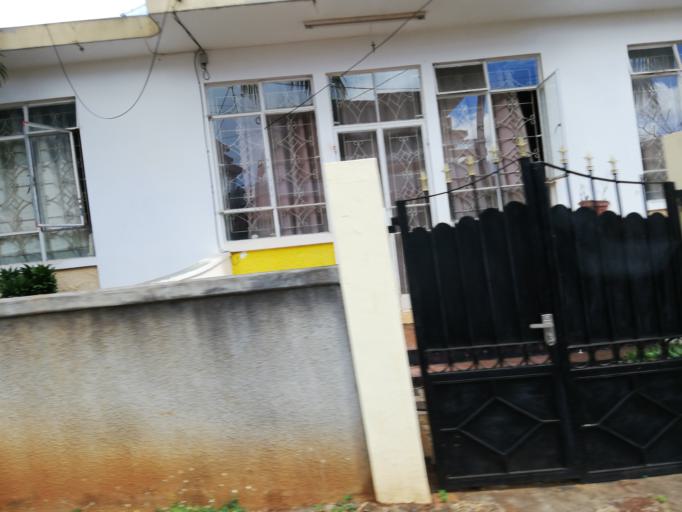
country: MU
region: Moka
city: Pailles
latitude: -20.1981
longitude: 57.4705
